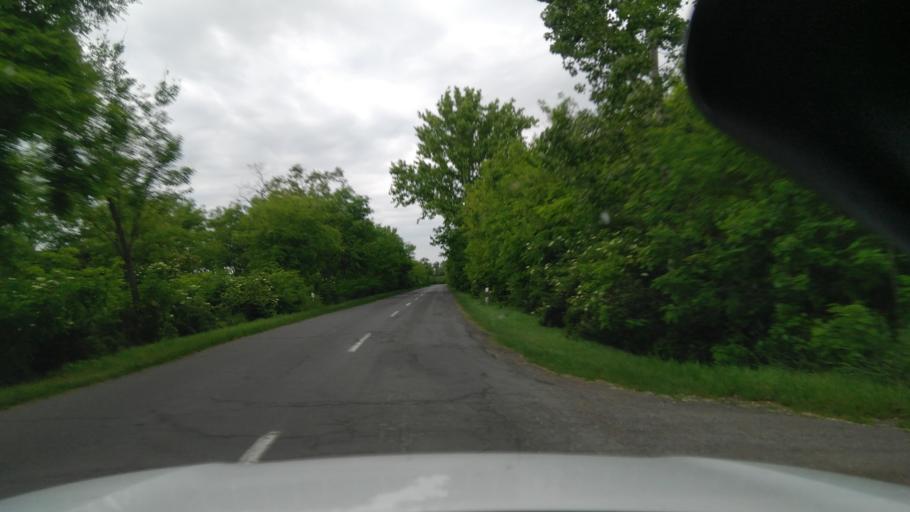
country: HU
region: Bekes
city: Bekescsaba
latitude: 46.6817
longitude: 21.1669
